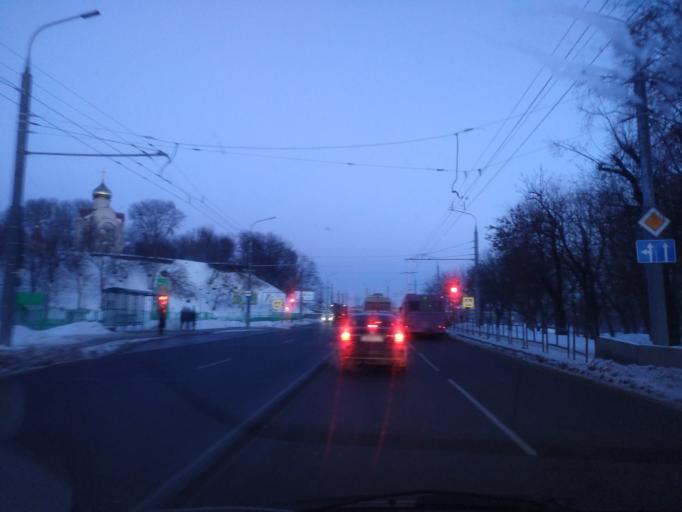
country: BY
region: Mogilev
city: Mahilyow
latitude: 53.8931
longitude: 30.3246
